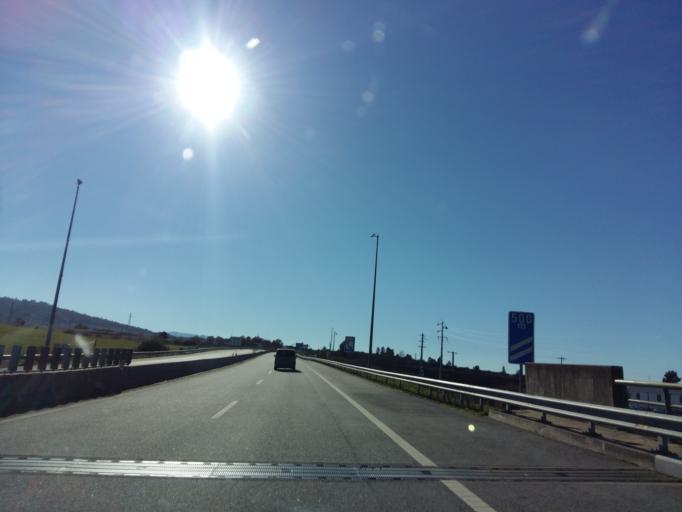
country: PT
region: Castelo Branco
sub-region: Covilha
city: Covilha
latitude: 40.2370
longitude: -7.4828
